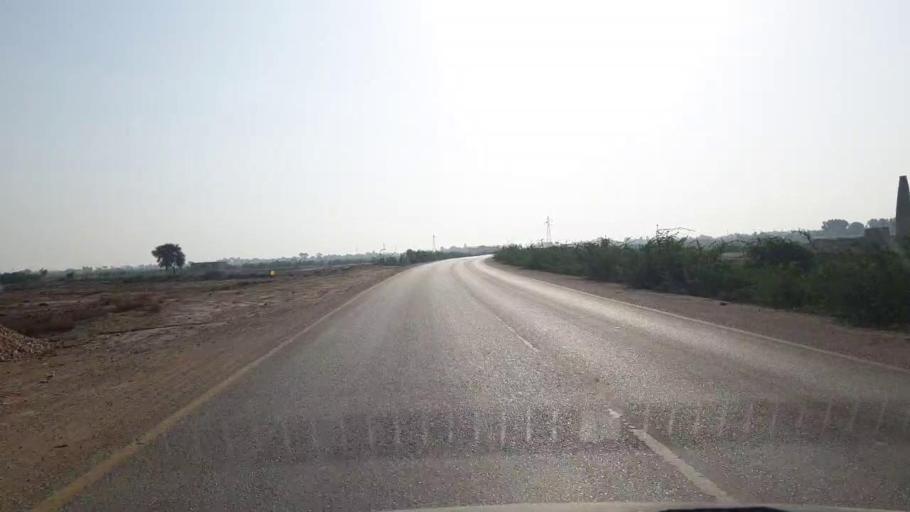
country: PK
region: Sindh
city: Badin
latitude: 24.6806
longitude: 68.8403
